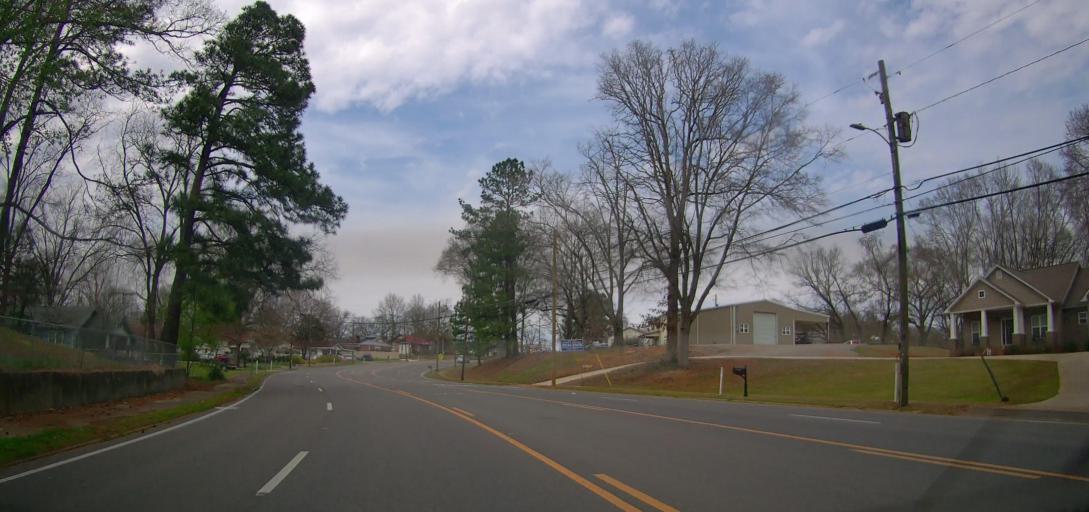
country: US
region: Alabama
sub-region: Marion County
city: Guin
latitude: 33.9704
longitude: -87.9154
